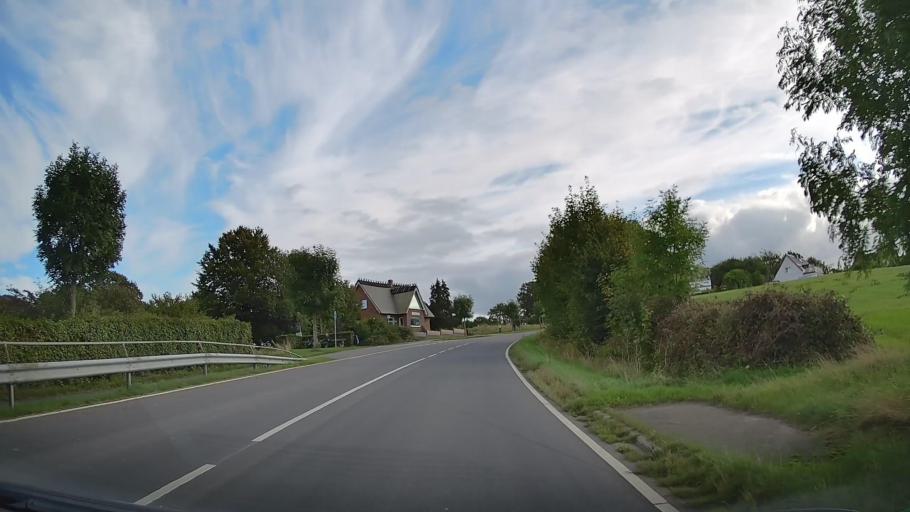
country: DE
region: Schleswig-Holstein
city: Westerholz
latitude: 54.8182
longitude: 9.6715
